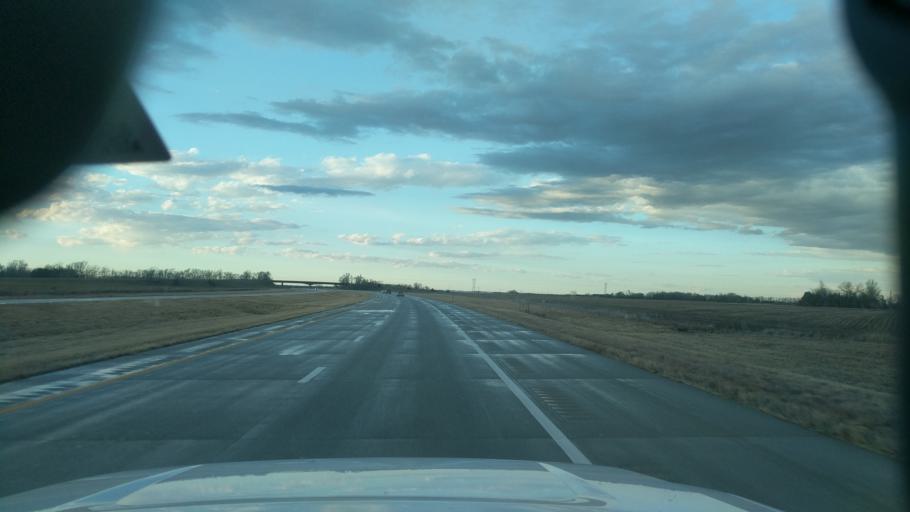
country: US
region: Kansas
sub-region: Harvey County
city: Hesston
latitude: 38.1685
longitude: -97.4397
